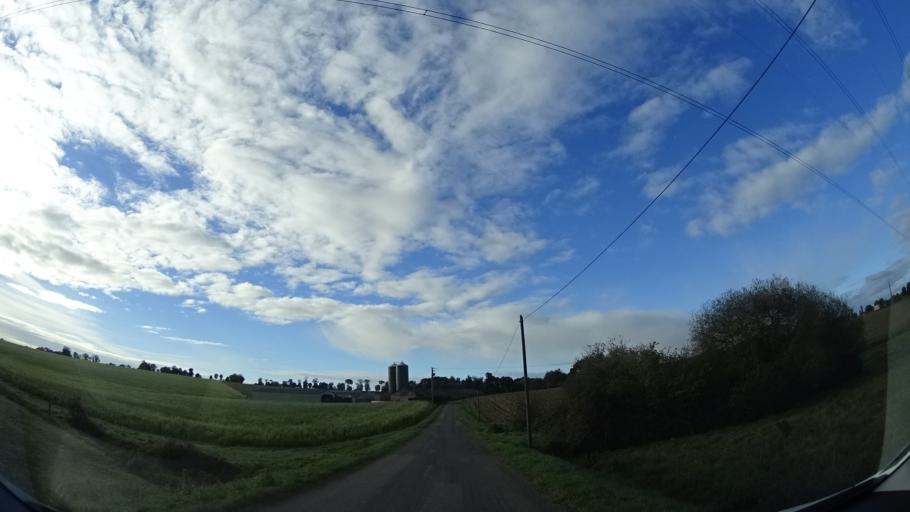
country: FR
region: Brittany
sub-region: Departement d'Ille-et-Vilaine
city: Geveze
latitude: 48.2012
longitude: -1.8095
